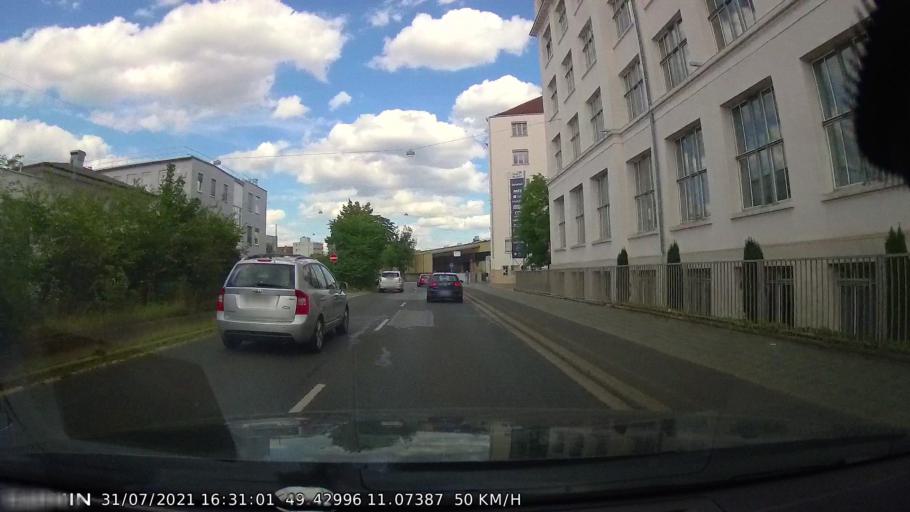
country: DE
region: Bavaria
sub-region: Regierungsbezirk Mittelfranken
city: Nuernberg
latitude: 49.4297
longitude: 11.0734
